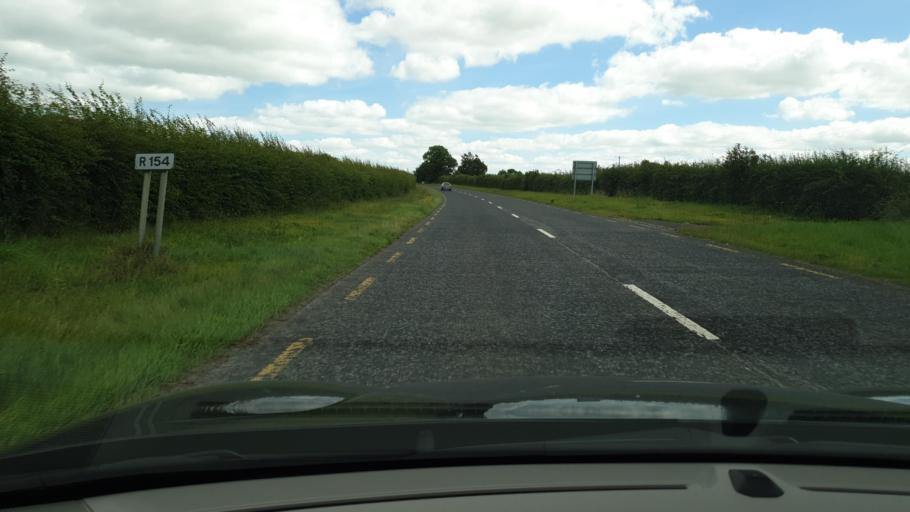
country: IE
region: Leinster
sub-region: An Mhi
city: Newtown Trim
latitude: 53.5358
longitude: -6.7075
